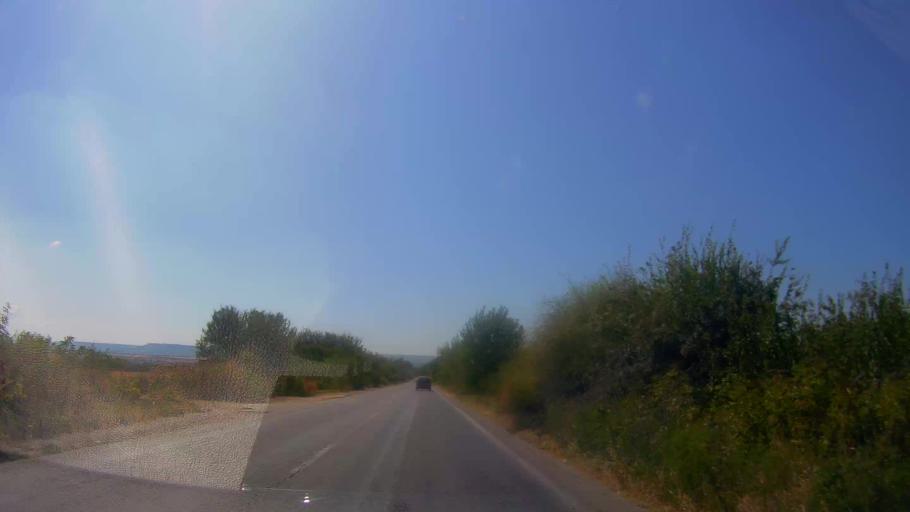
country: BG
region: Veliko Turnovo
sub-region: Obshtina Gorna Oryakhovitsa
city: Purvomaytsi
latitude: 43.2250
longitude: 25.6378
